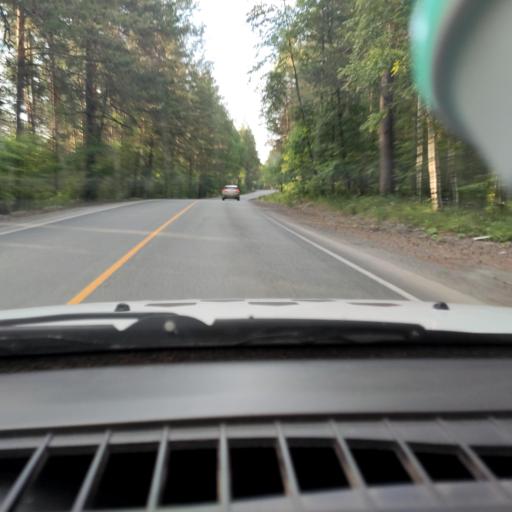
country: RU
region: Chelyabinsk
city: Turgoyak
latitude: 55.2587
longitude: 60.1977
